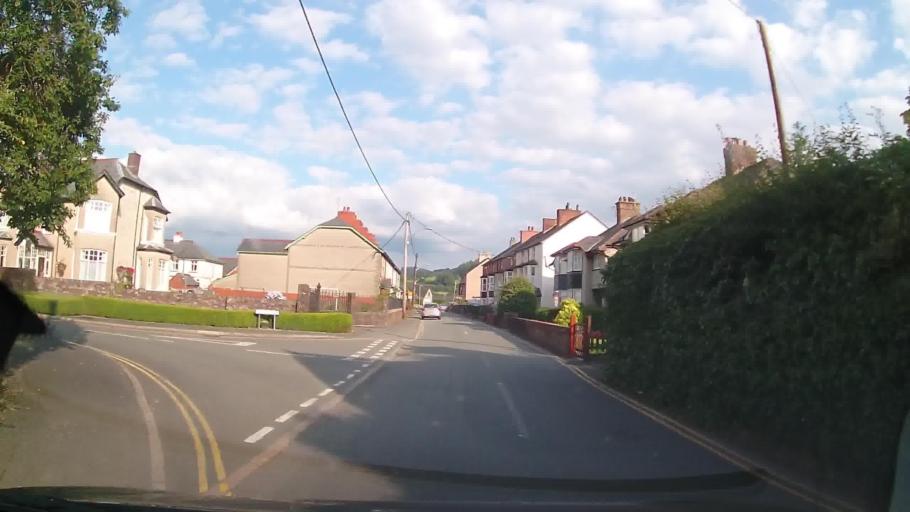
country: GB
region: Wales
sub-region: Gwynedd
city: Bala
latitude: 52.9091
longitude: -3.5969
